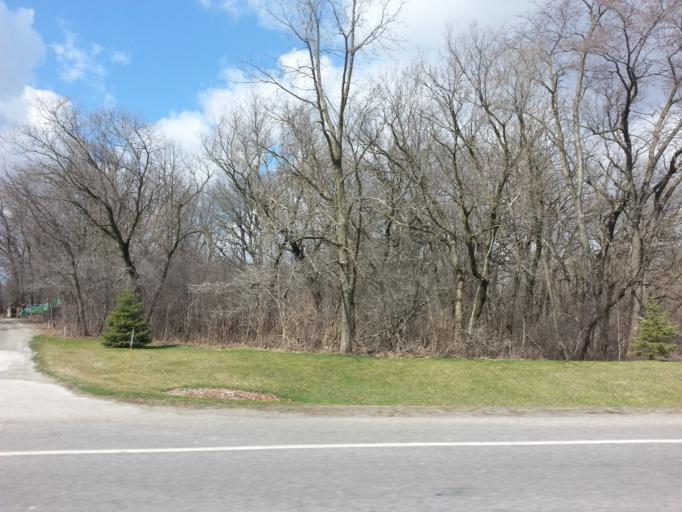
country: US
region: Minnesota
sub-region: Dodge County
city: Mantorville
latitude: 44.0798
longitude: -92.7127
